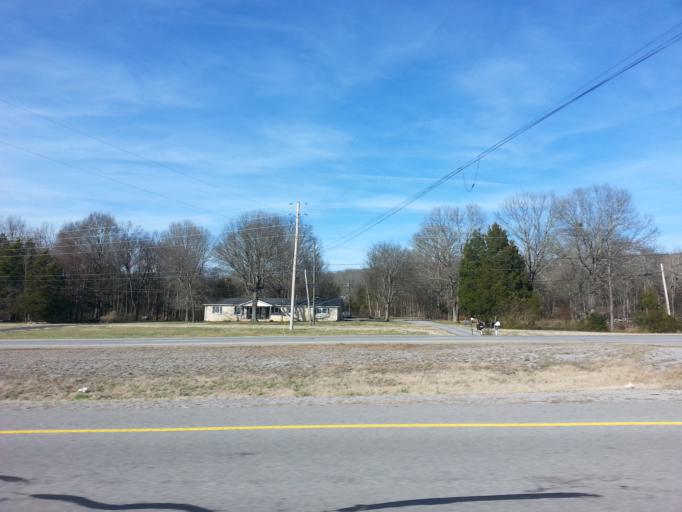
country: US
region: Tennessee
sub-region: Rutherford County
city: Murfreesboro
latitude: 35.8183
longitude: -86.2335
